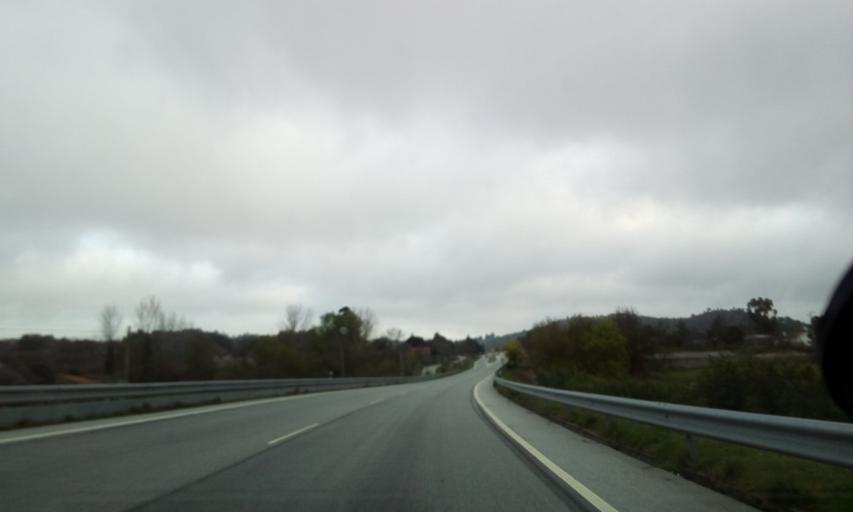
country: PT
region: Guarda
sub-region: Fornos de Algodres
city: Fornos de Algodres
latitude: 40.6340
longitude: -7.5003
